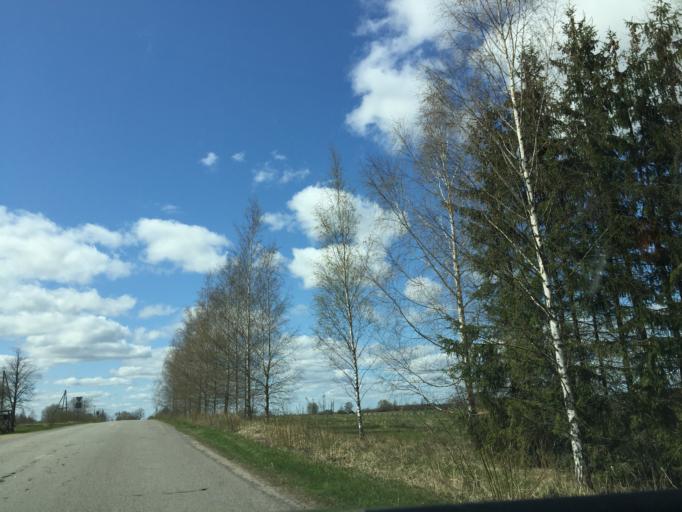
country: LV
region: Vilanu
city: Vilani
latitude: 56.7205
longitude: 27.1151
